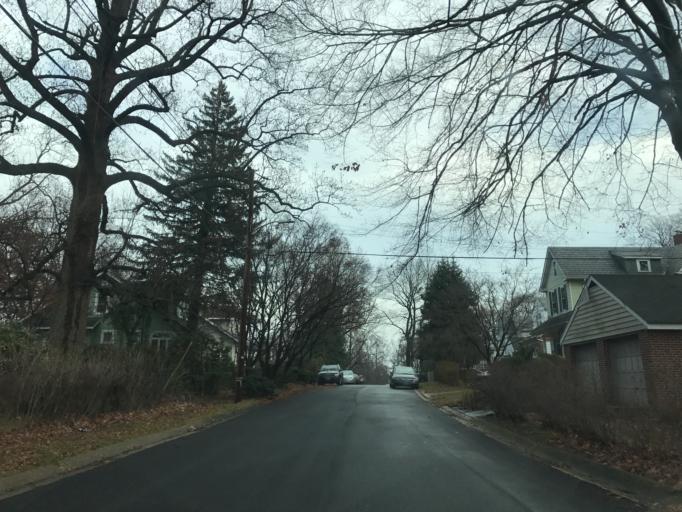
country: US
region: Maryland
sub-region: Baltimore County
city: Overlea
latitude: 39.3556
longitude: -76.5398
